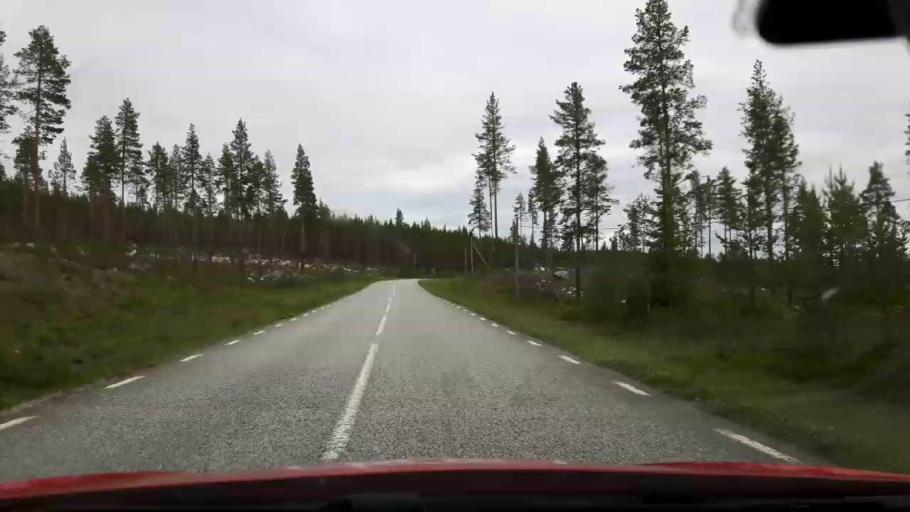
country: SE
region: Jaemtland
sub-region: Stroemsunds Kommun
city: Stroemsund
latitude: 63.3600
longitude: 15.7168
